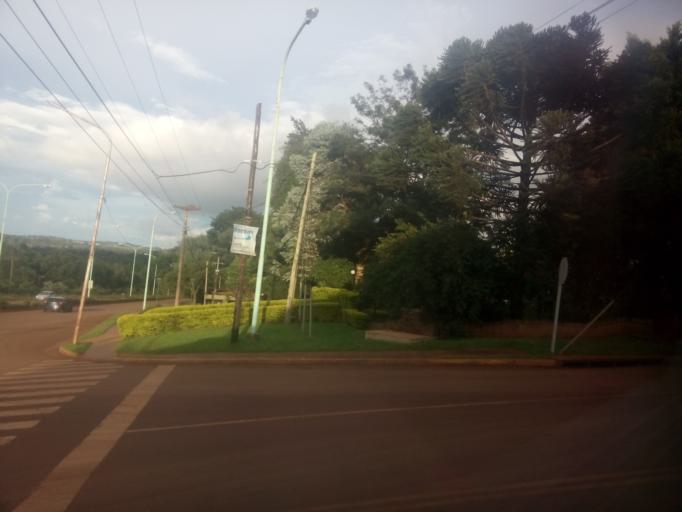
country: AR
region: Misiones
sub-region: Departamento de Obera
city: Obera
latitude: -27.4892
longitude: -55.1466
